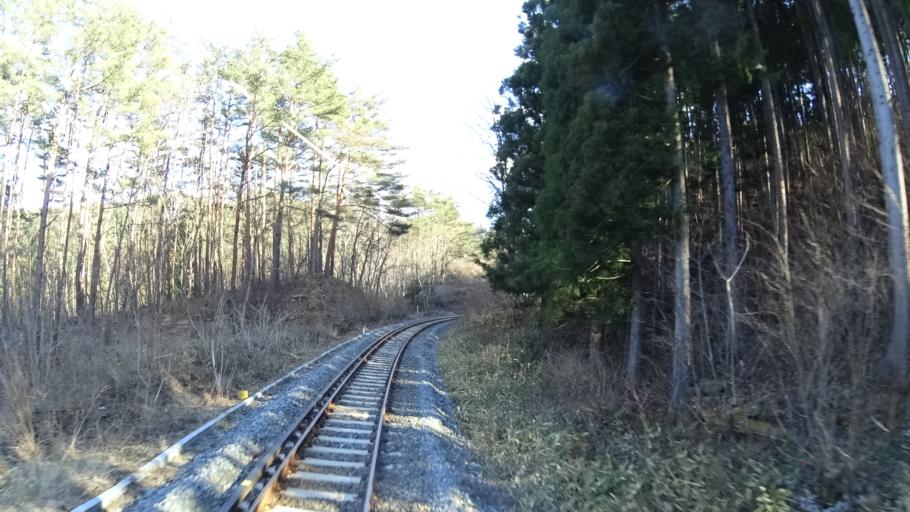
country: JP
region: Iwate
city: Yamada
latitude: 39.5008
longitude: 141.9288
